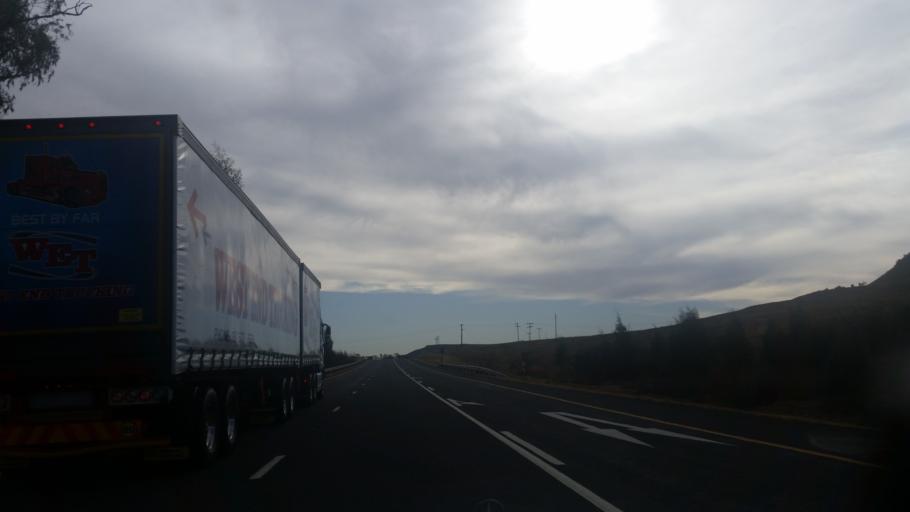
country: ZA
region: Orange Free State
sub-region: Thabo Mofutsanyana District Municipality
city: Phuthaditjhaba
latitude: -28.3133
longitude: 28.7270
